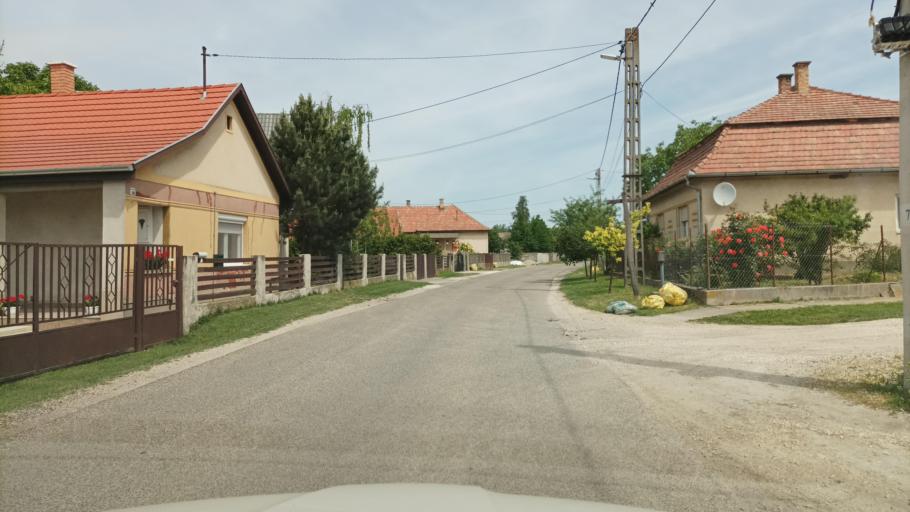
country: HU
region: Fejer
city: Adony
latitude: 47.0933
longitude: 18.9264
